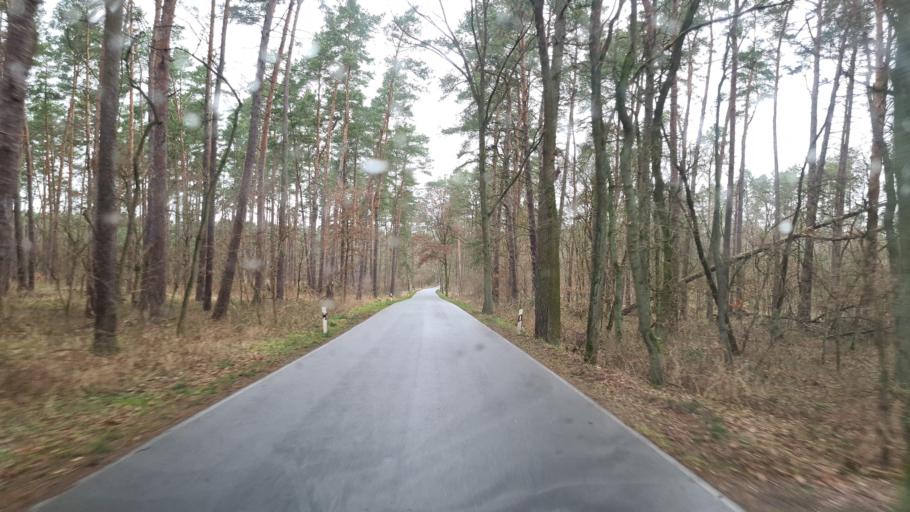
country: DE
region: Brandenburg
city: Gransee
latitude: 52.8860
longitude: 13.2064
